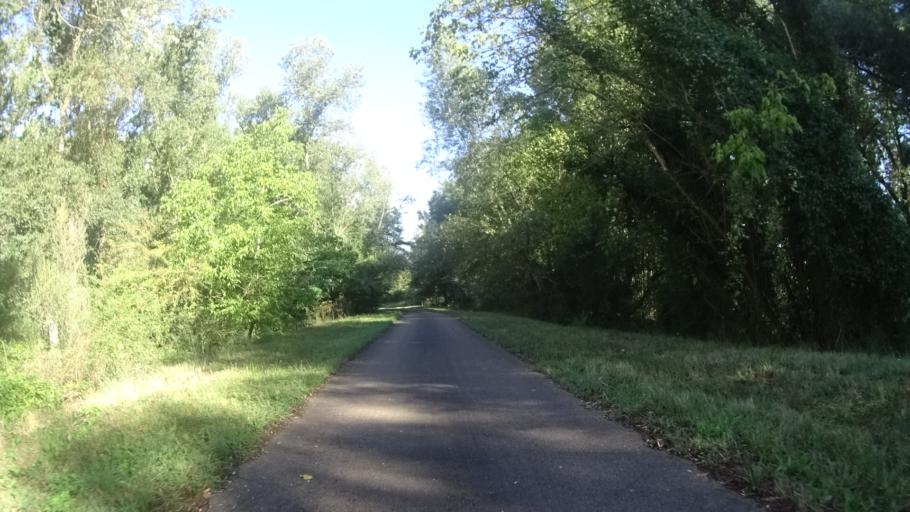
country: FR
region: Bourgogne
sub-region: Departement de la Nievre
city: Pouilly-sur-Loire
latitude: 47.3054
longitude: 2.9124
